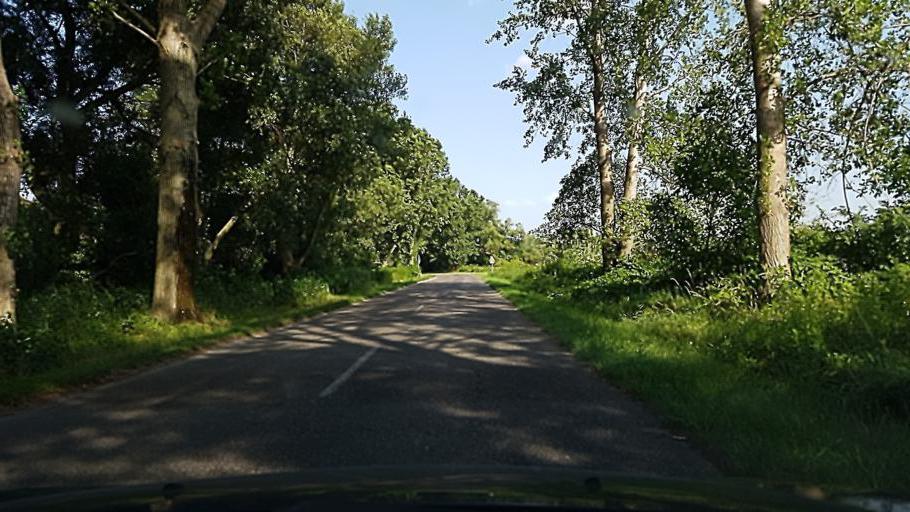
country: HU
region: Komarom-Esztergom
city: Kesztolc
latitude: 47.7020
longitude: 18.7753
